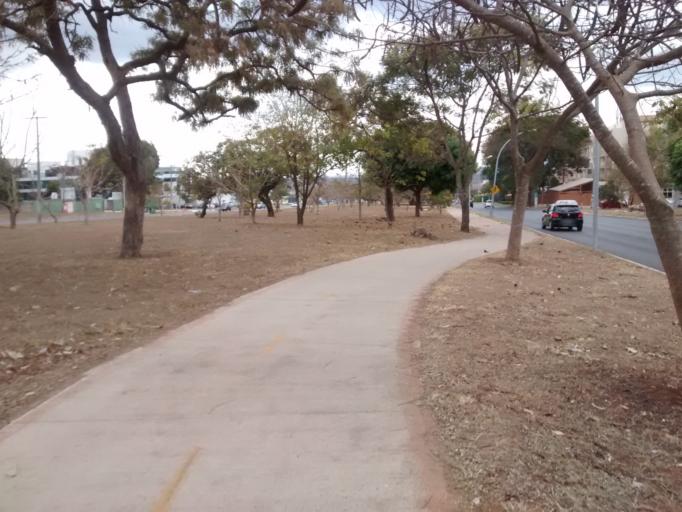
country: BR
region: Federal District
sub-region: Brasilia
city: Brasilia
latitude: -15.7446
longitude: -47.9003
